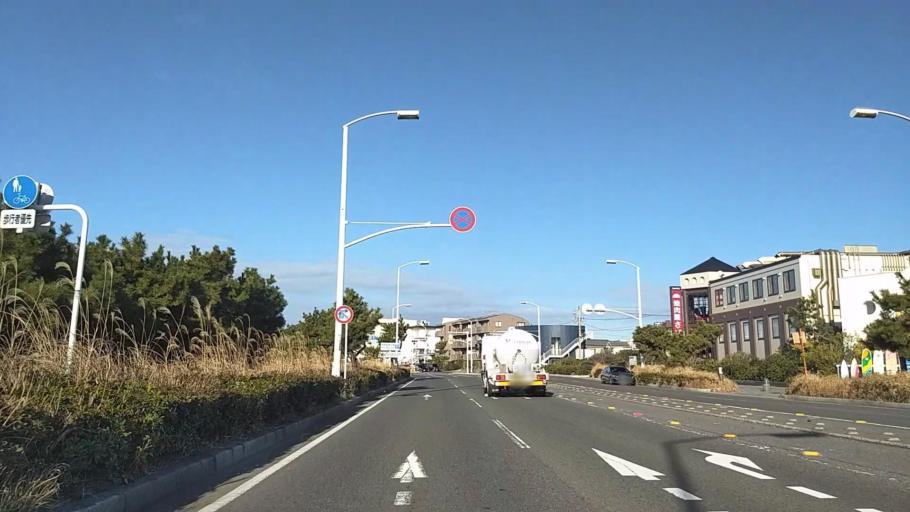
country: JP
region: Kanagawa
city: Fujisawa
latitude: 35.3164
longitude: 139.4718
